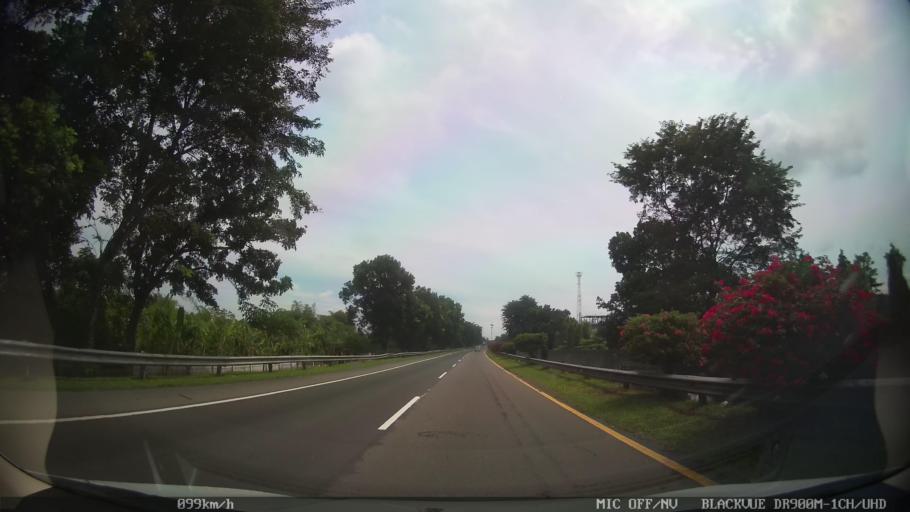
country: ID
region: North Sumatra
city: Labuhan Deli
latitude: 3.6767
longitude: 98.6802
